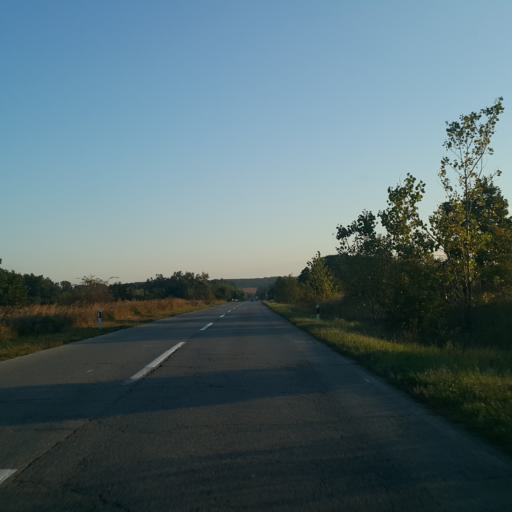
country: RS
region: Central Serbia
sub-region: Borski Okrug
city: Negotin
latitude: 44.1434
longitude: 22.3513
